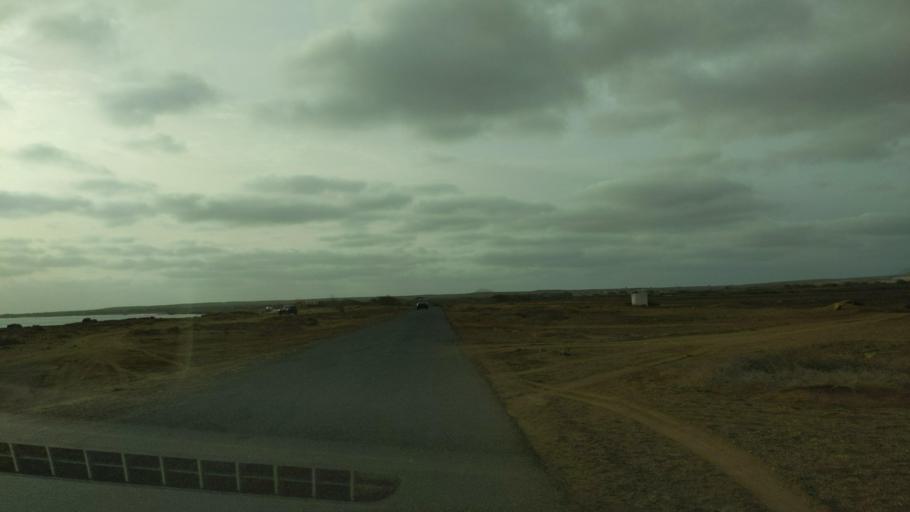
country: CV
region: Sal
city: Espargos
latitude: 16.6858
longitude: -22.9377
